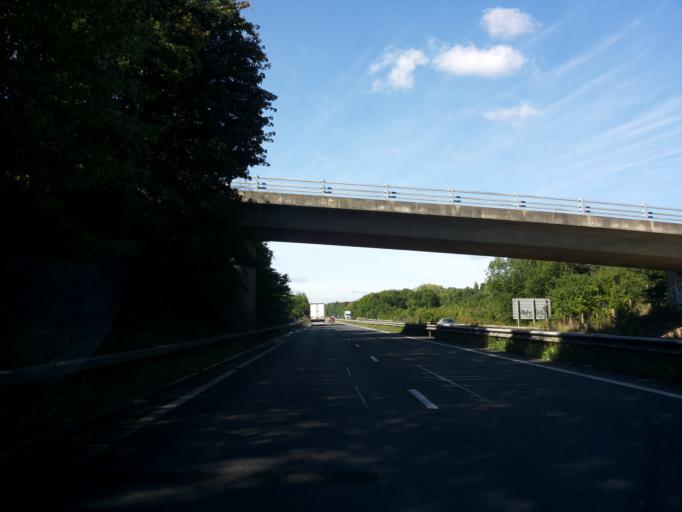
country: GB
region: England
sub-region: Kent
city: Blean
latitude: 51.2800
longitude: 1.0400
